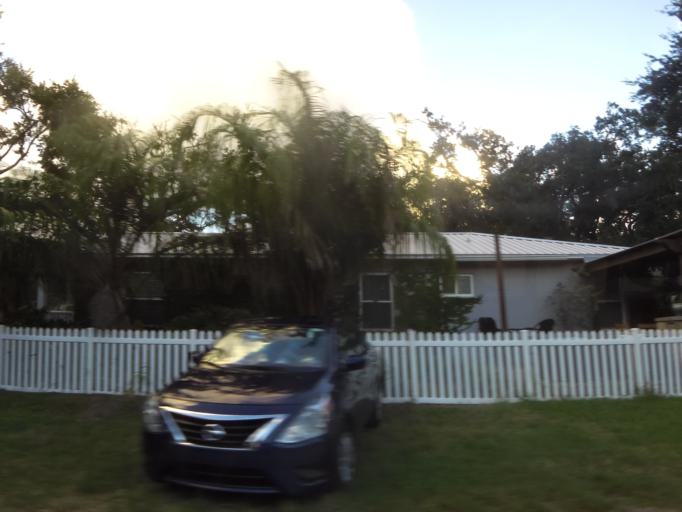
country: US
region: Florida
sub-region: Saint Johns County
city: Villano Beach
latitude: 29.9558
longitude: -81.3118
